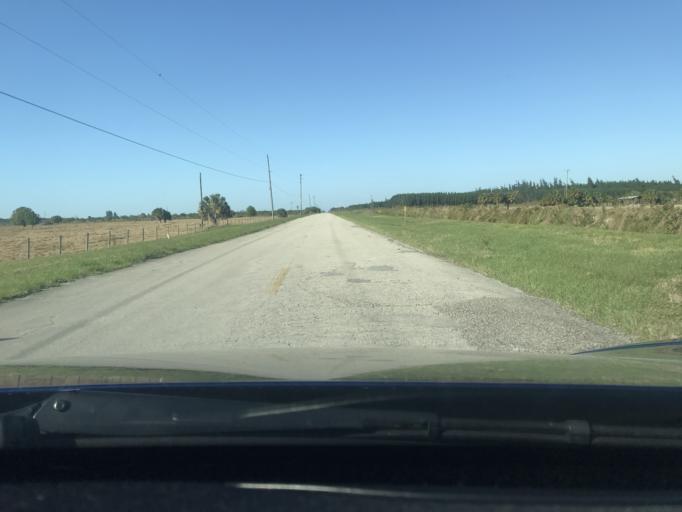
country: US
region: Florida
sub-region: Saint Lucie County
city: Fort Pierce South
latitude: 27.3928
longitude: -80.4976
